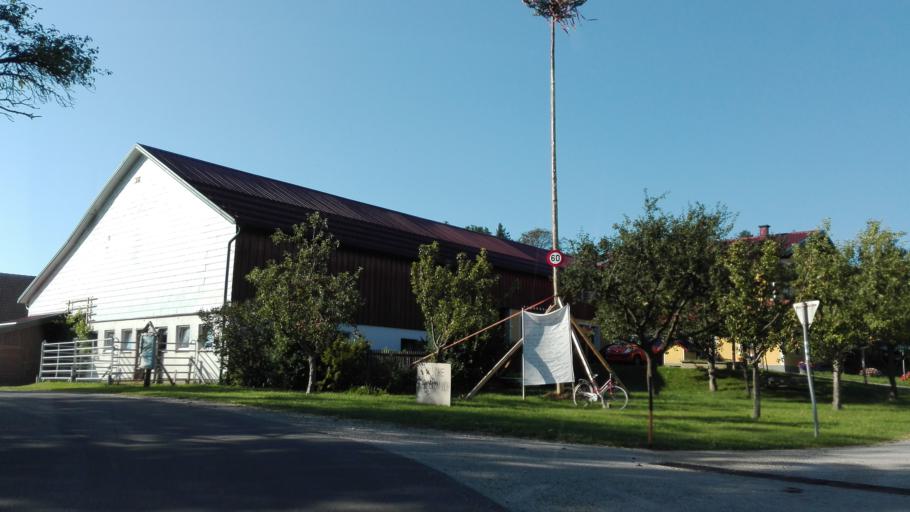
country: AT
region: Lower Austria
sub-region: Politischer Bezirk Sankt Polten
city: Stossing
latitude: 48.0934
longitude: 15.8254
